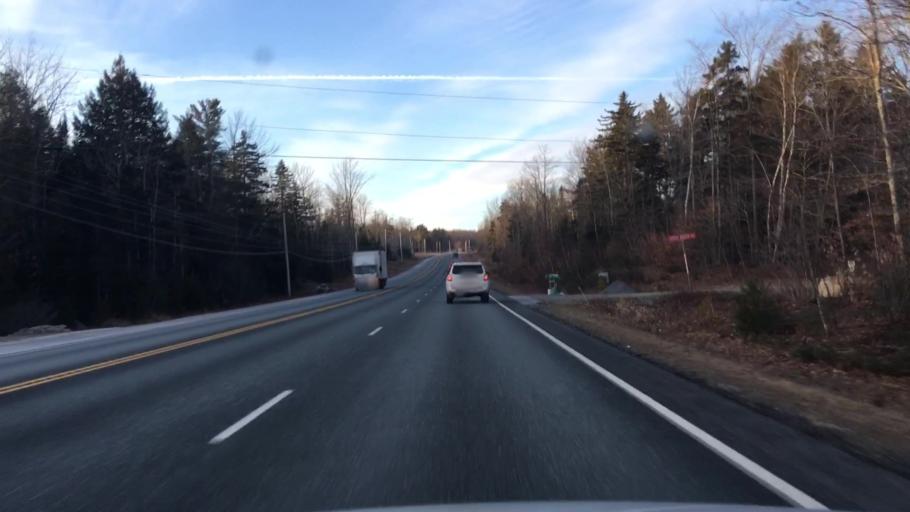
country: US
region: Maine
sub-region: Hancock County
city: Dedham
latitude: 44.6395
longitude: -68.5505
